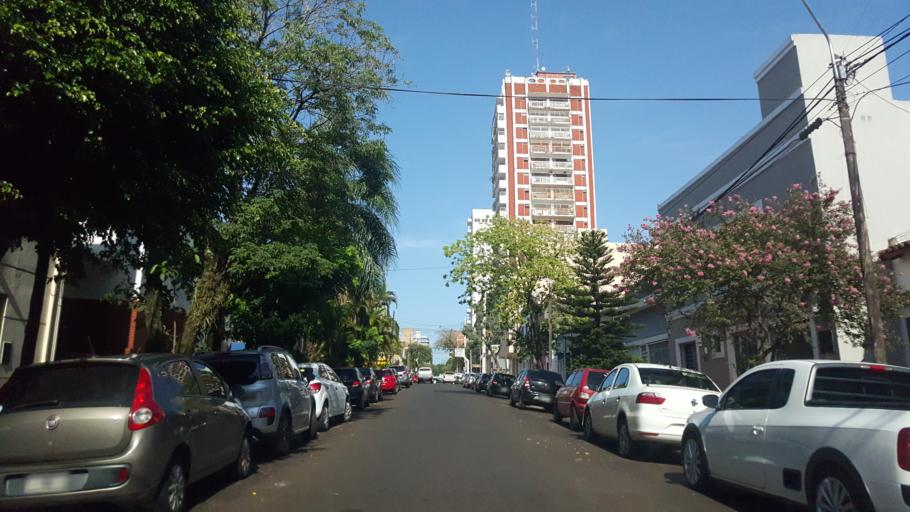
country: AR
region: Misiones
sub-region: Departamento de Capital
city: Posadas
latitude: -27.3726
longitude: -55.8943
